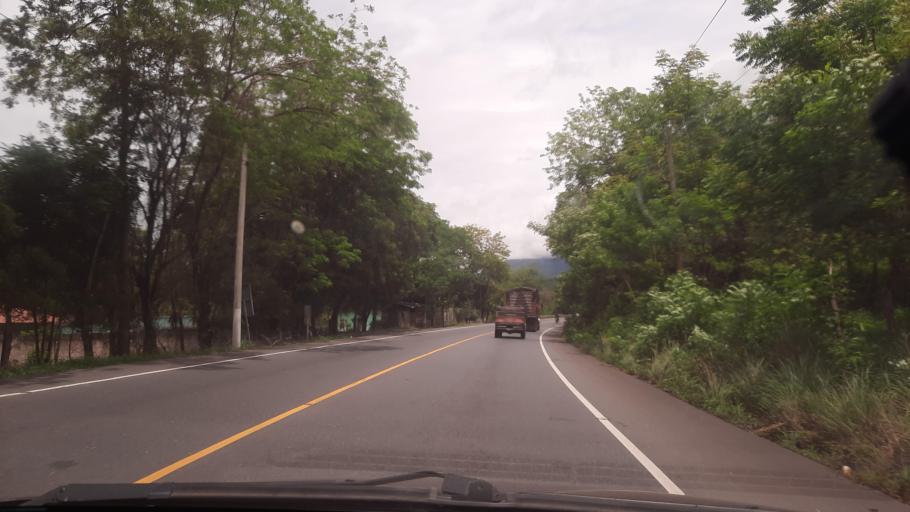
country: GT
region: Zacapa
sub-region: Municipio de Zacapa
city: Gualan
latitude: 15.1975
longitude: -89.2648
